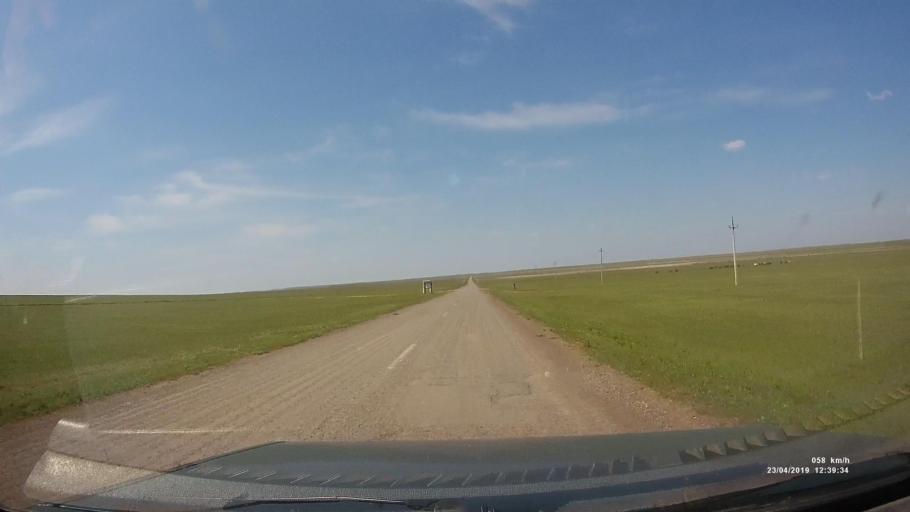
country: RU
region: Kalmykiya
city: Yashalta
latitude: 46.4350
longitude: 42.7072
